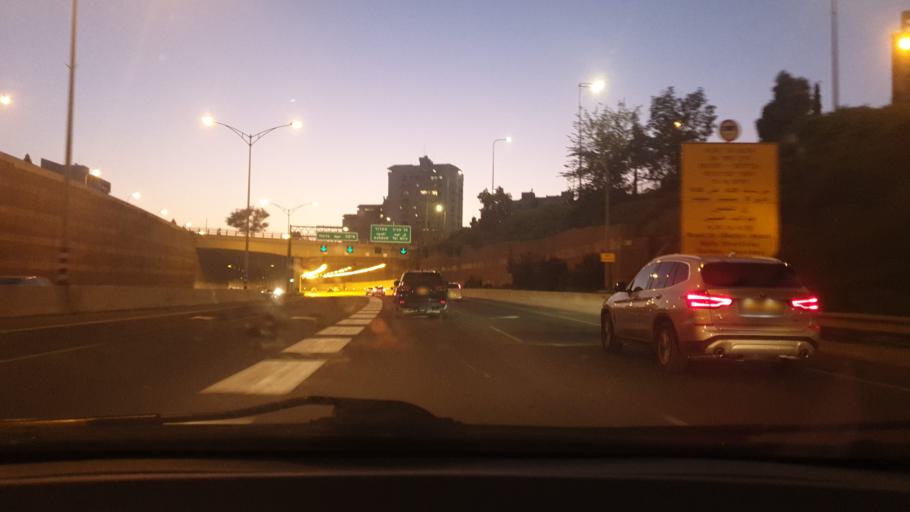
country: IL
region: Tel Aviv
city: Giv`at Shemu'el
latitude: 32.0673
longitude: 34.8495
